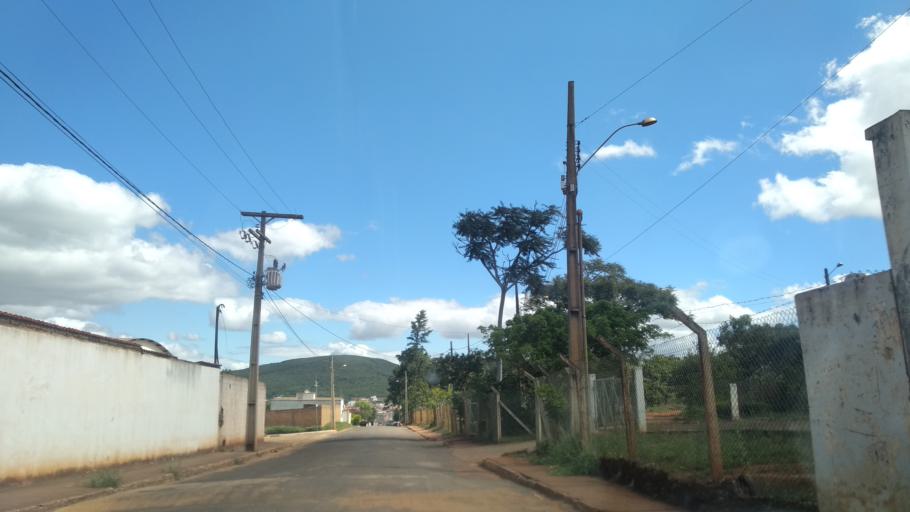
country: BR
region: Bahia
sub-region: Caetite
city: Caetite
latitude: -14.0566
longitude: -42.4869
